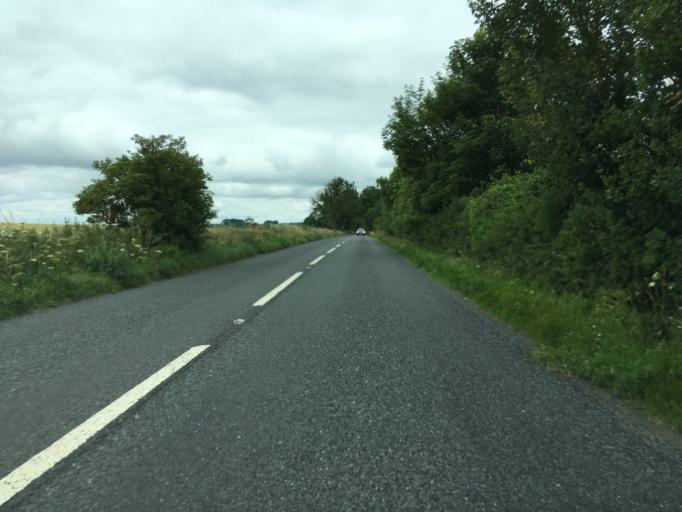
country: GB
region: England
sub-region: Gloucestershire
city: Westfield
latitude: 51.8885
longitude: -1.8548
